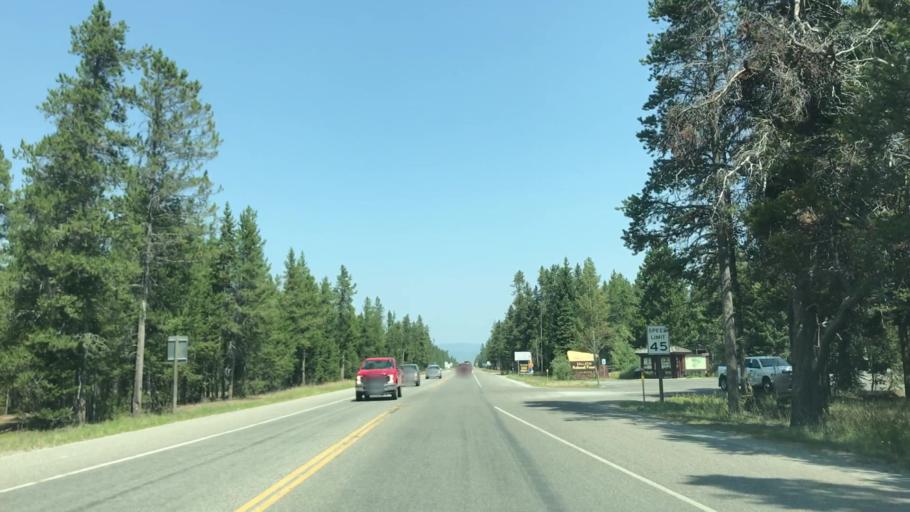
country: US
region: Montana
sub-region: Gallatin County
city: West Yellowstone
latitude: 44.6662
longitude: -111.0999
